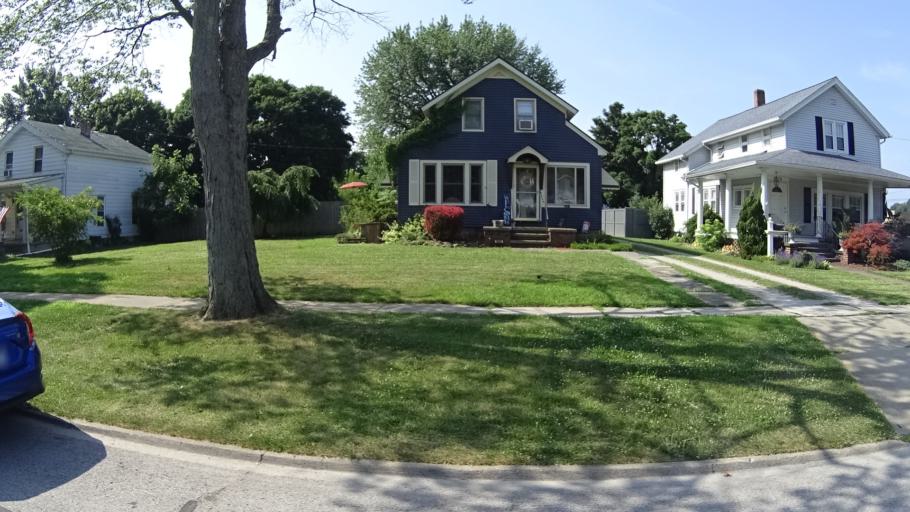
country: US
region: Ohio
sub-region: Lorain County
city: Vermilion
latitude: 41.4191
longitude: -82.3669
